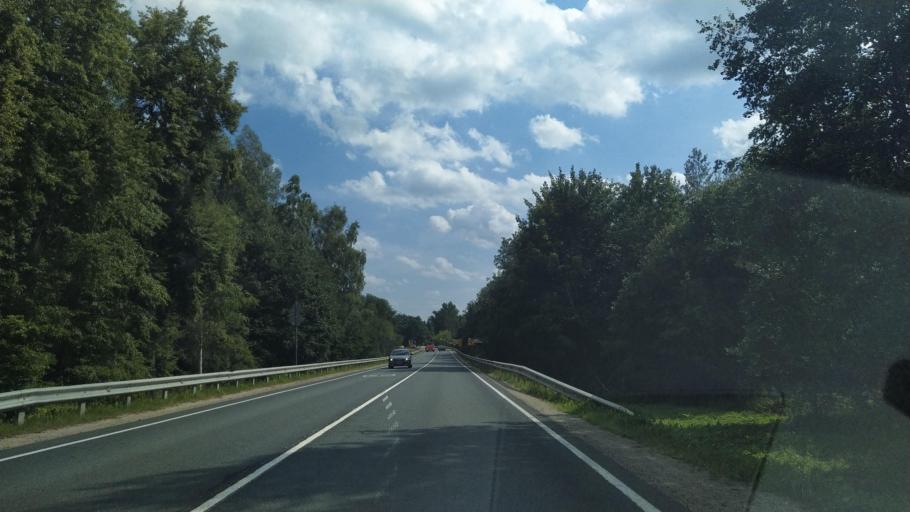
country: RU
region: Pskov
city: Pskov
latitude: 57.7155
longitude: 28.8485
